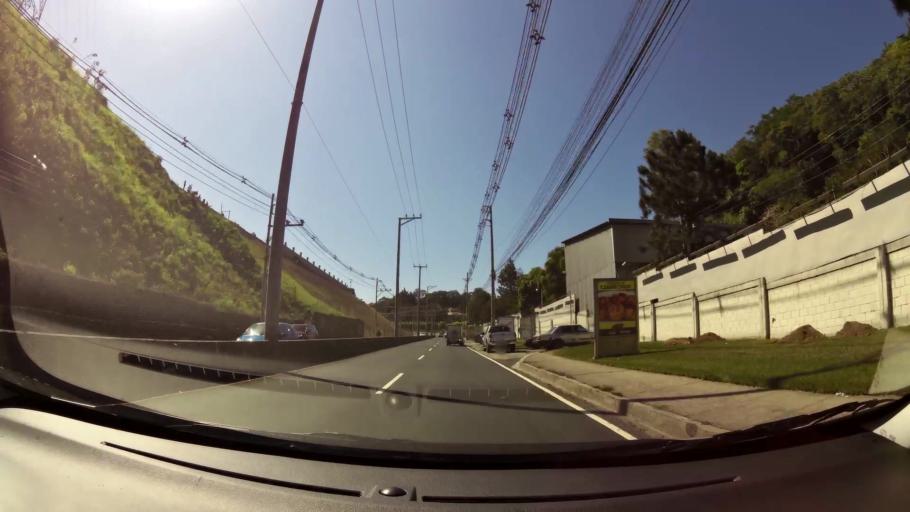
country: SV
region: La Libertad
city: Santa Tecla
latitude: 13.6613
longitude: -89.2788
